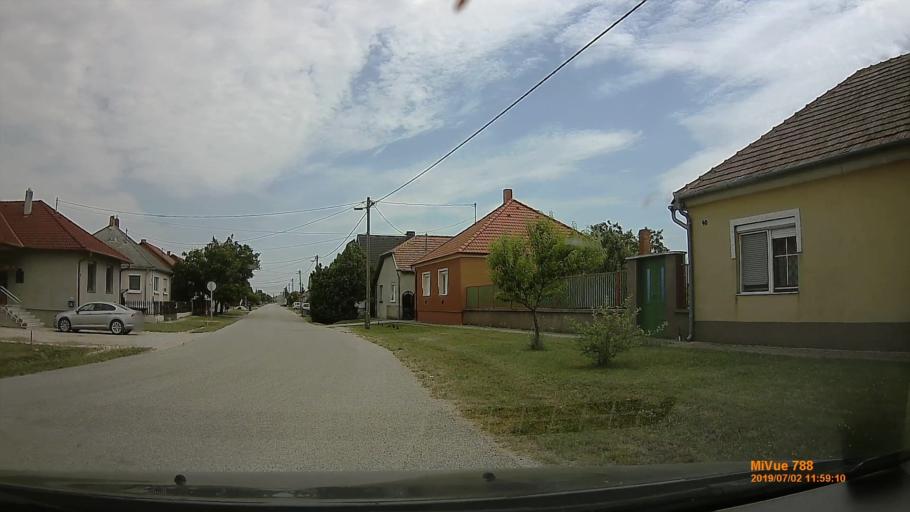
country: HU
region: Gyor-Moson-Sopron
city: Janossomorja
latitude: 47.8472
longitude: 17.1737
